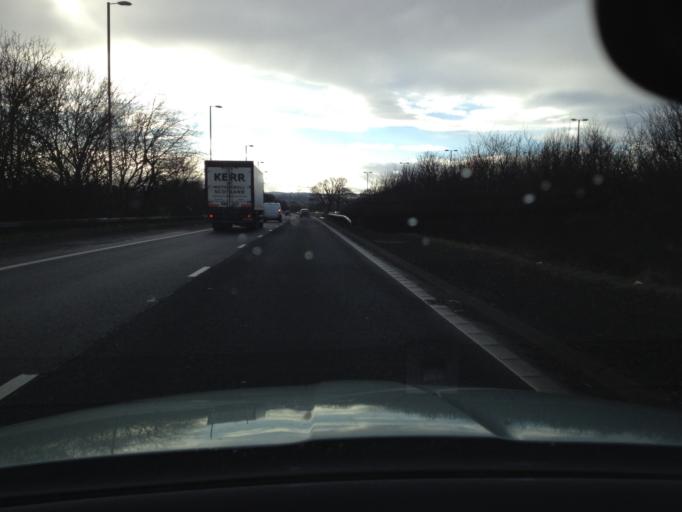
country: GB
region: Scotland
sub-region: Edinburgh
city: Newbridge
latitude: 55.9250
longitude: -3.4128
